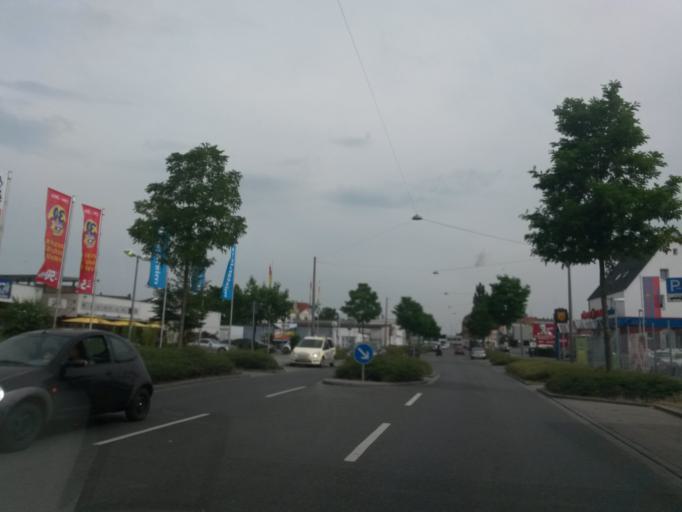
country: DE
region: Bavaria
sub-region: Regierungsbezirk Mittelfranken
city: Furth
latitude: 49.4585
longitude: 11.0078
